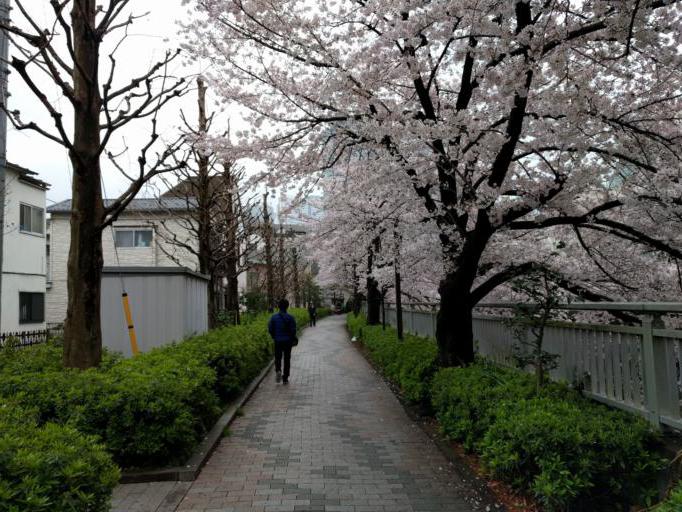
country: JP
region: Tokyo
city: Tokyo
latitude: 35.7008
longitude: 139.6880
